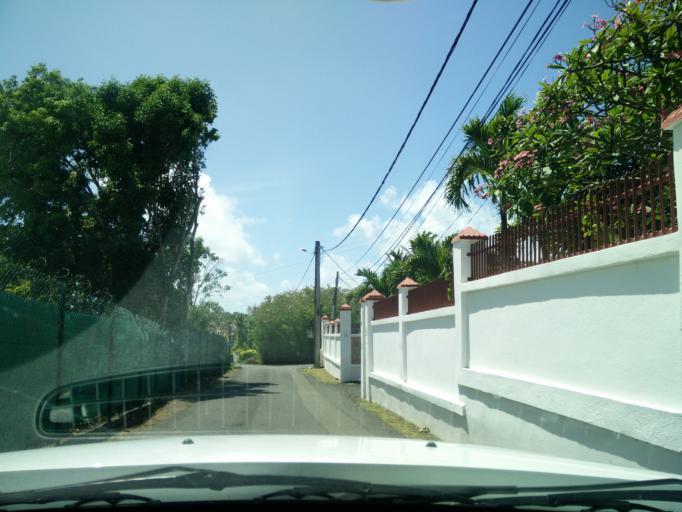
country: GP
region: Guadeloupe
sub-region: Guadeloupe
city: Sainte-Anne
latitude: 16.2463
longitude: -61.3440
